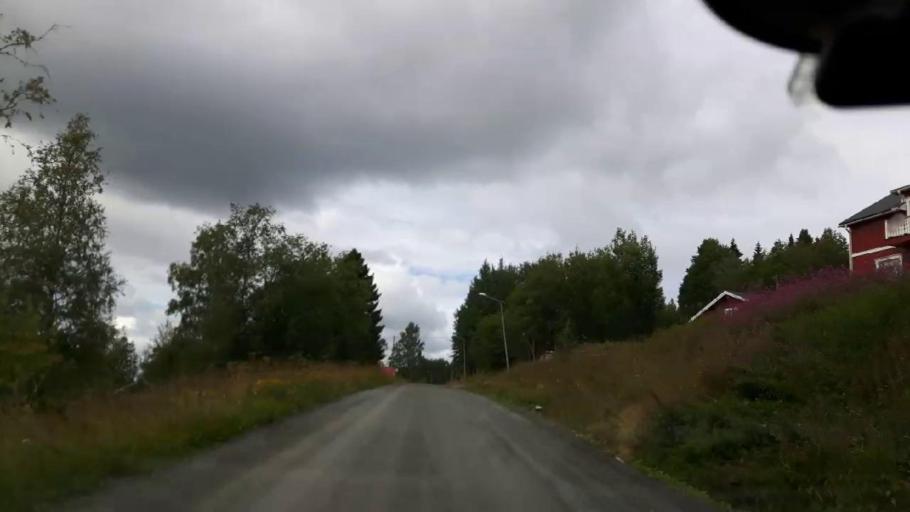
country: SE
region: Jaemtland
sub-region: Krokoms Kommun
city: Valla
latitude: 63.4905
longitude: 13.9854
